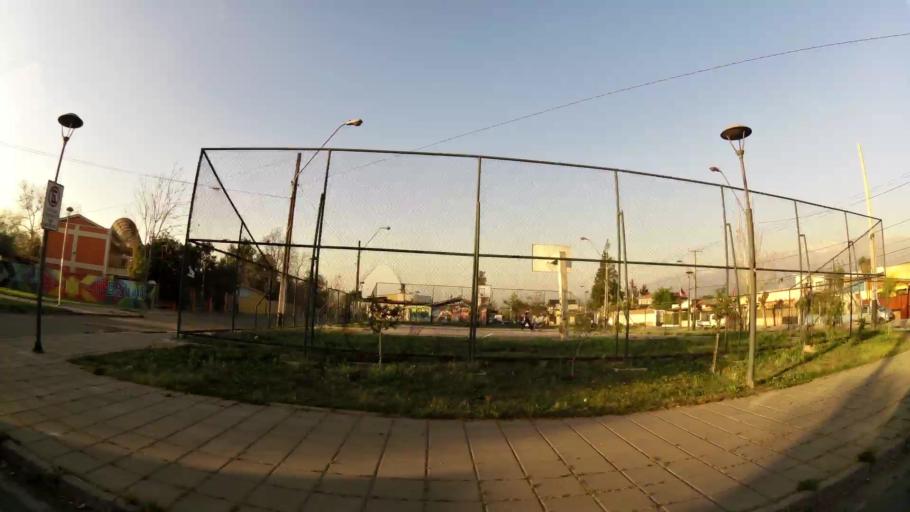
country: CL
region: Santiago Metropolitan
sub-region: Provincia de Santiago
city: Santiago
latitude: -33.5174
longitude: -70.6209
